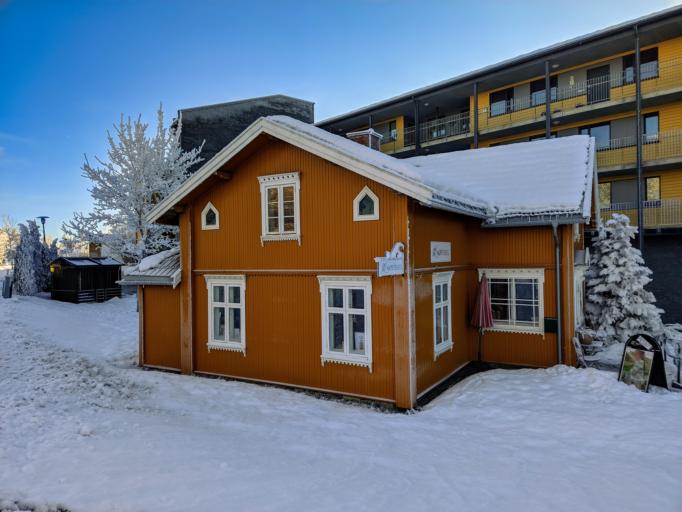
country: NO
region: Akershus
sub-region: Gjerdrum
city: Ask
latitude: 60.0711
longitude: 11.0359
